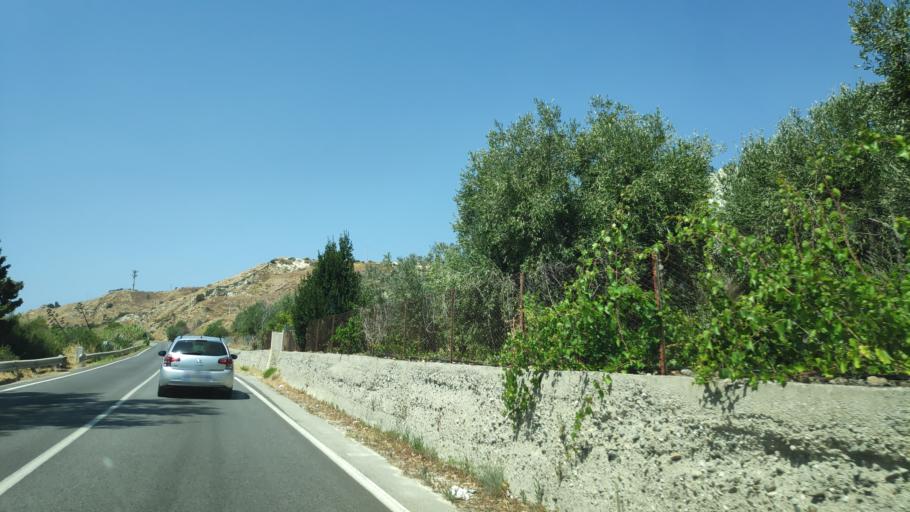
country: IT
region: Calabria
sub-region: Provincia di Reggio Calabria
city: Palizzi Marina
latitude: 37.9196
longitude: 16.0060
